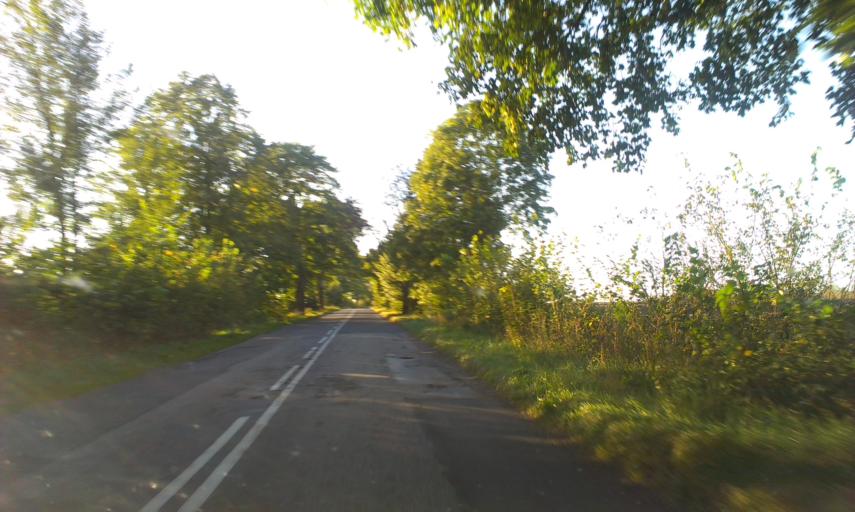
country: PL
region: Pomeranian Voivodeship
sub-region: Powiat czluchowski
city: Rzeczenica
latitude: 53.6415
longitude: 17.1526
